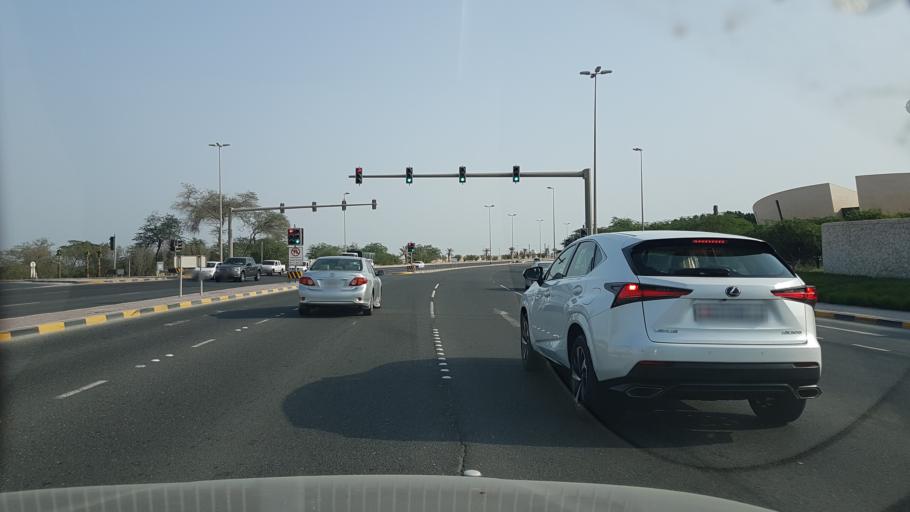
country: BH
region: Central Governorate
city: Dar Kulayb
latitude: 26.0703
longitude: 50.5242
